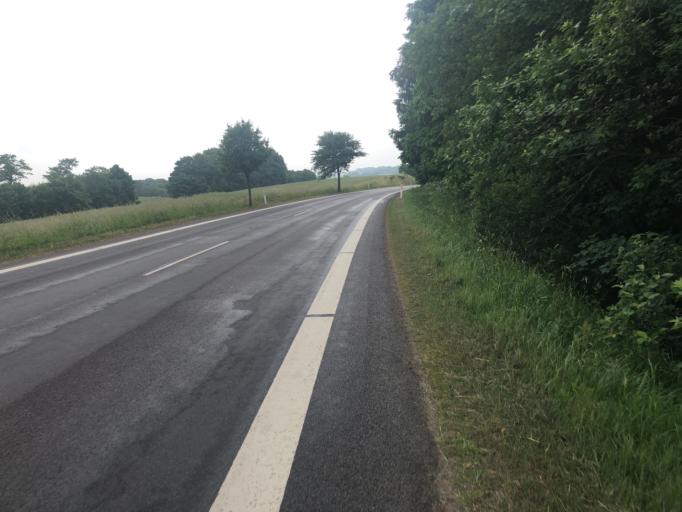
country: DK
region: Capital Region
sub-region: Bornholm Kommune
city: Akirkeby
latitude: 55.1525
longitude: 14.8937
